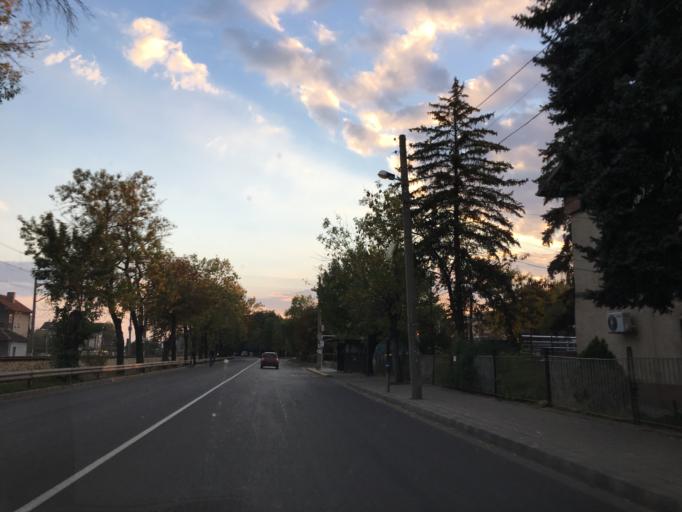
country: BG
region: Sofia-Capital
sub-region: Stolichna Obshtina
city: Sofia
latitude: 42.8031
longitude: 23.3440
